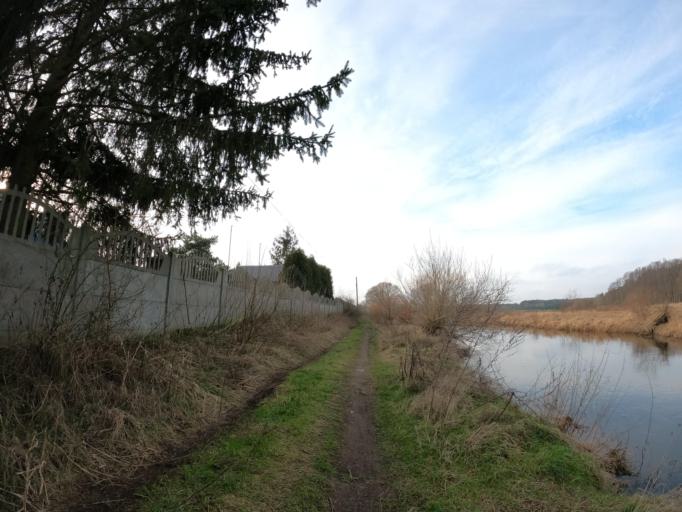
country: PL
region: West Pomeranian Voivodeship
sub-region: Powiat goleniowski
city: Goleniow
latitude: 53.5655
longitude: 14.7912
